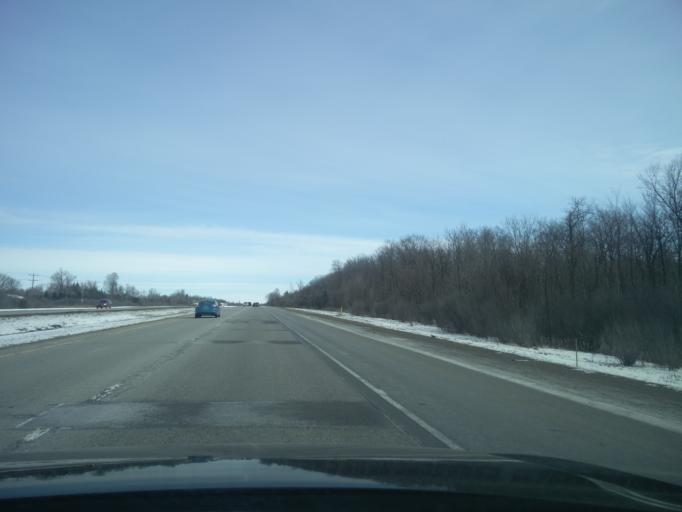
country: CA
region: Ontario
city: Prescott
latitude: 44.6805
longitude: -75.5928
